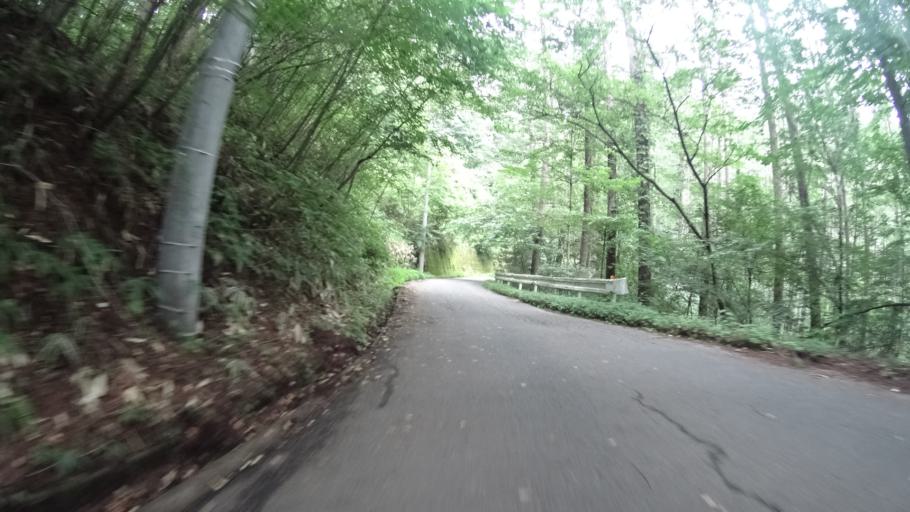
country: JP
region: Yamanashi
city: Nirasaki
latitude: 35.8985
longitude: 138.4200
